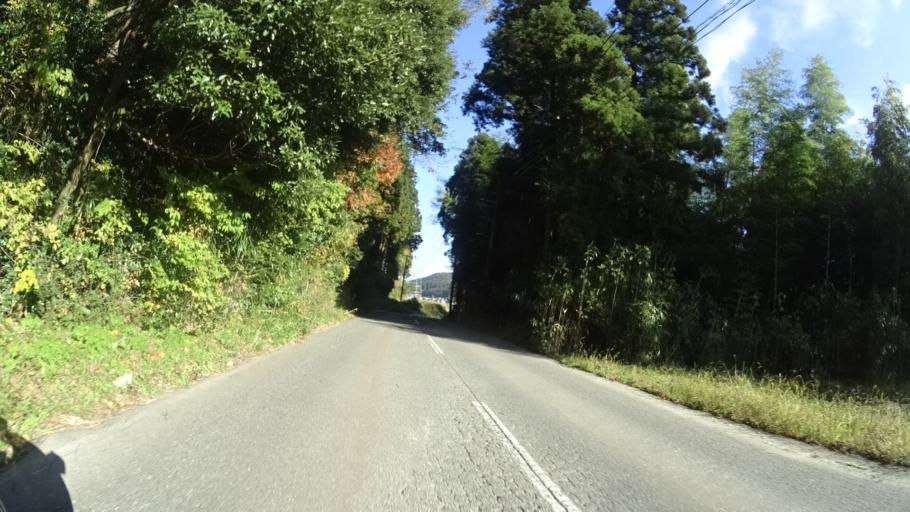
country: JP
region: Ishikawa
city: Komatsu
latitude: 36.2613
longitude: 136.3921
